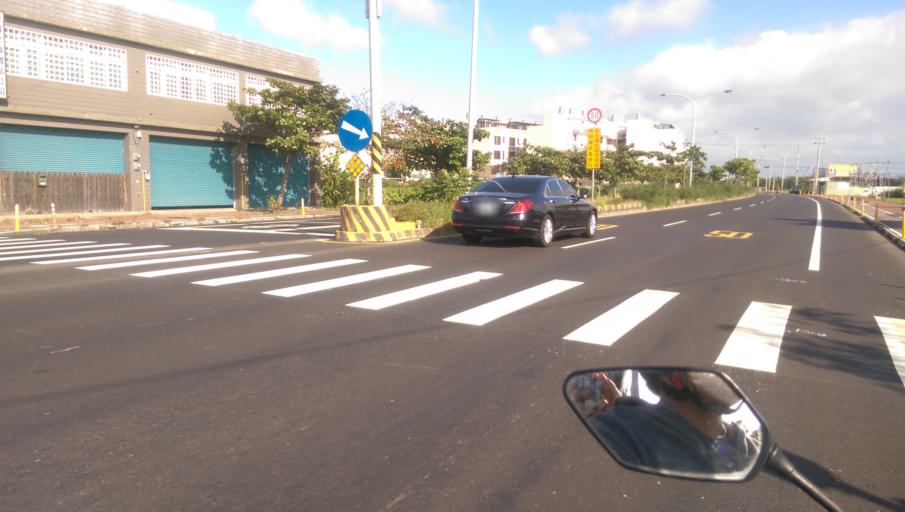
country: TW
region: Taiwan
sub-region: Hsinchu
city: Hsinchu
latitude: 24.8346
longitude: 120.9428
